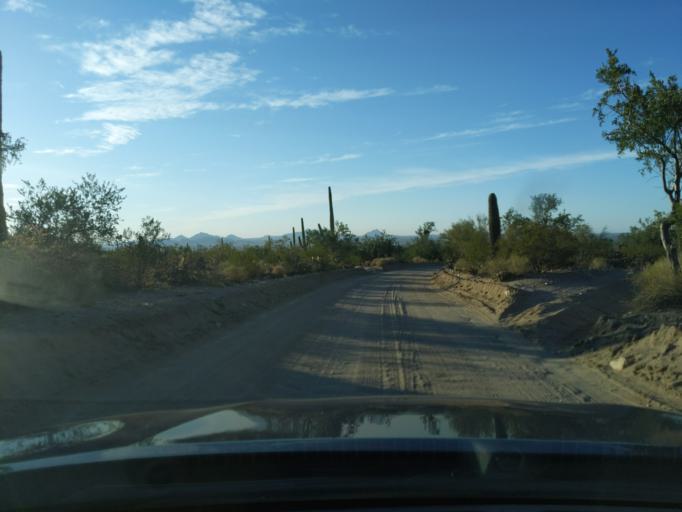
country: US
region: Arizona
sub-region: Pima County
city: Picture Rocks
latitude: 32.2871
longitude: -111.1888
